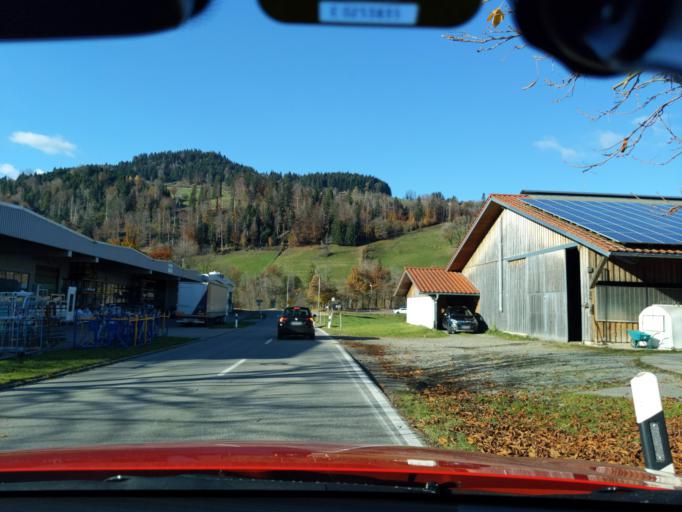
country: DE
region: Bavaria
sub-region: Swabia
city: Oberstaufen
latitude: 47.5412
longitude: 10.0161
